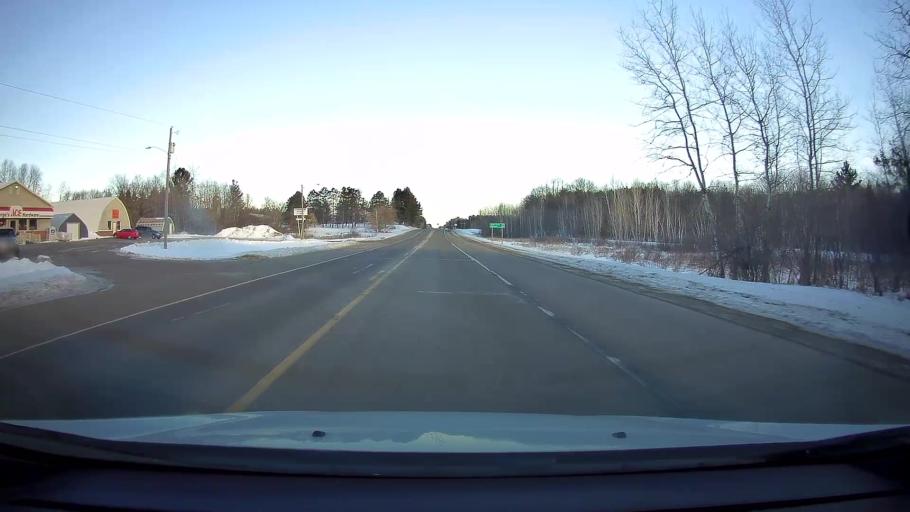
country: US
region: Wisconsin
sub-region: Barron County
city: Cumberland
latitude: 45.5529
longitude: -92.0172
